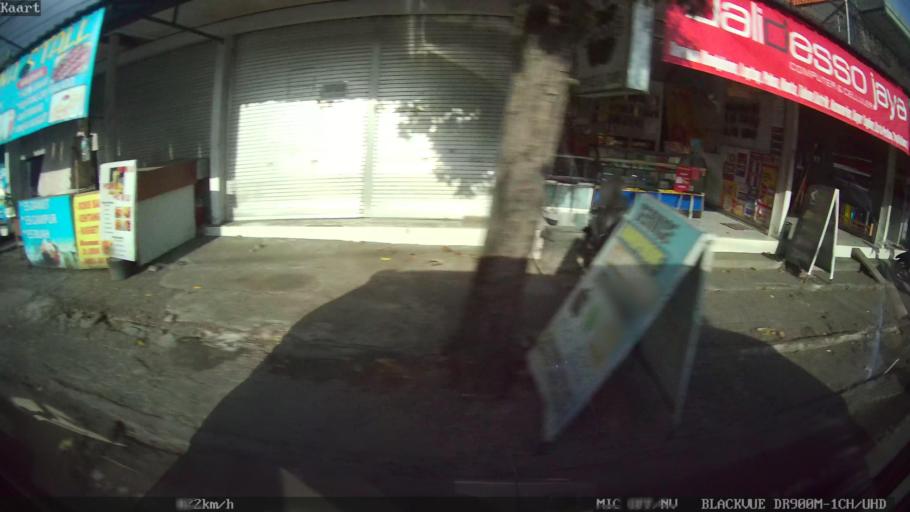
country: ID
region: Bali
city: Banjar Batur
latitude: -8.5917
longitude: 115.2155
